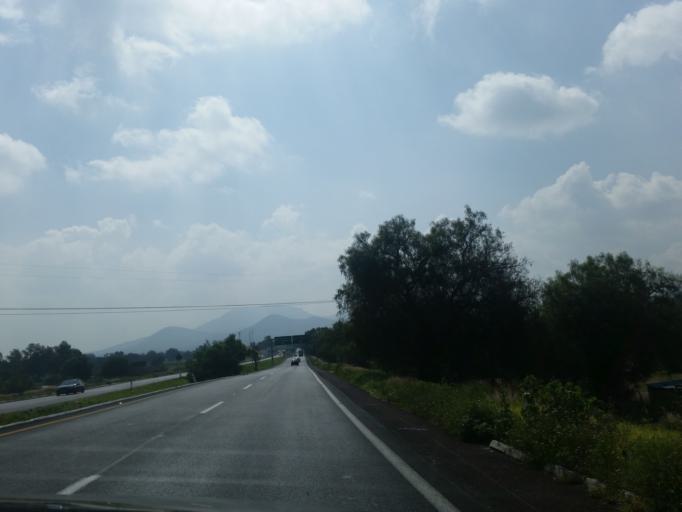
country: MX
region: Mexico
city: Acolman
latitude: 19.6283
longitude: -98.9262
